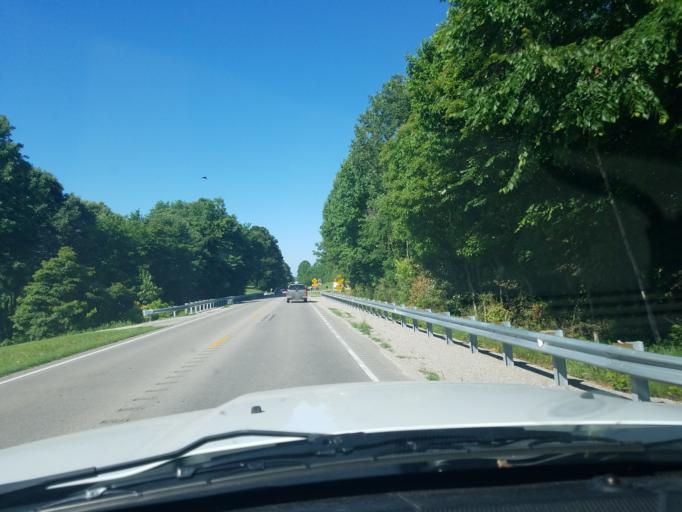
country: US
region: Kentucky
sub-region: Barren County
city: Glasgow
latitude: 36.9439
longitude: -85.9758
